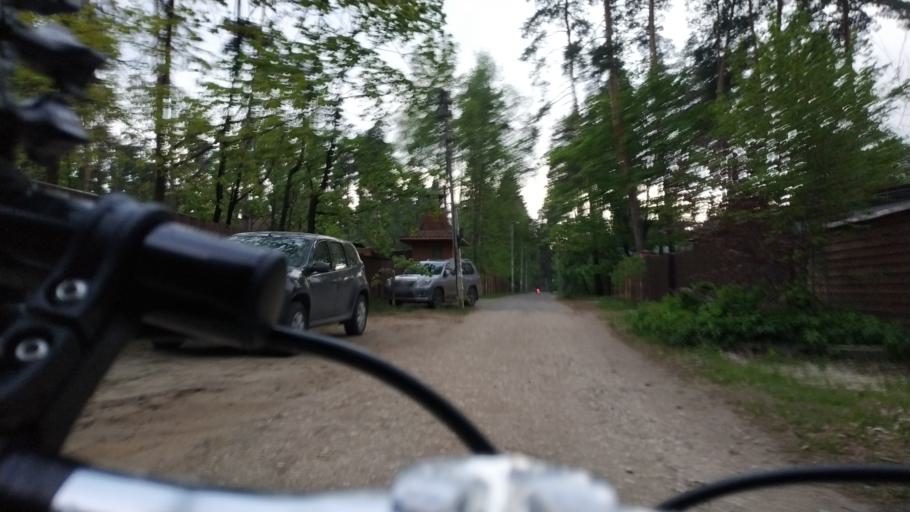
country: RU
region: Moskovskaya
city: Kratovo
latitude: 55.6116
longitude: 38.1674
